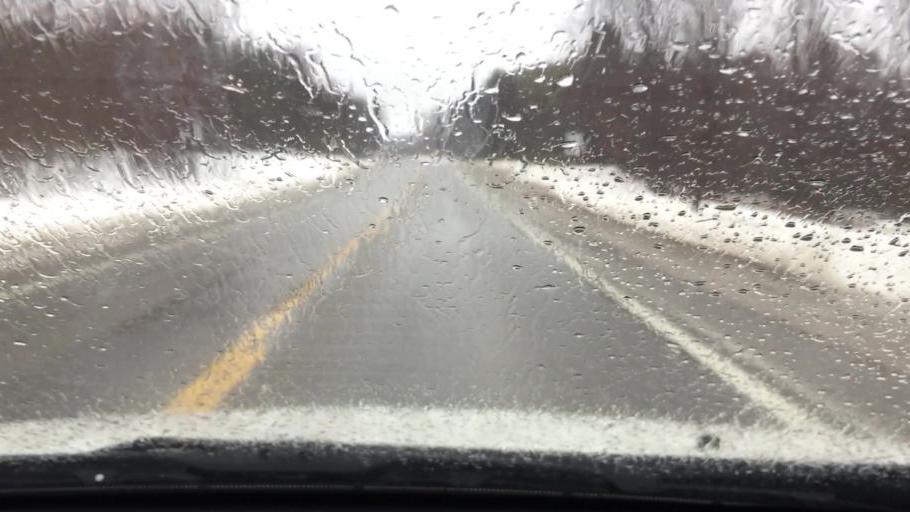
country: US
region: Michigan
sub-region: Charlevoix County
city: East Jordan
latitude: 45.1900
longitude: -85.1646
